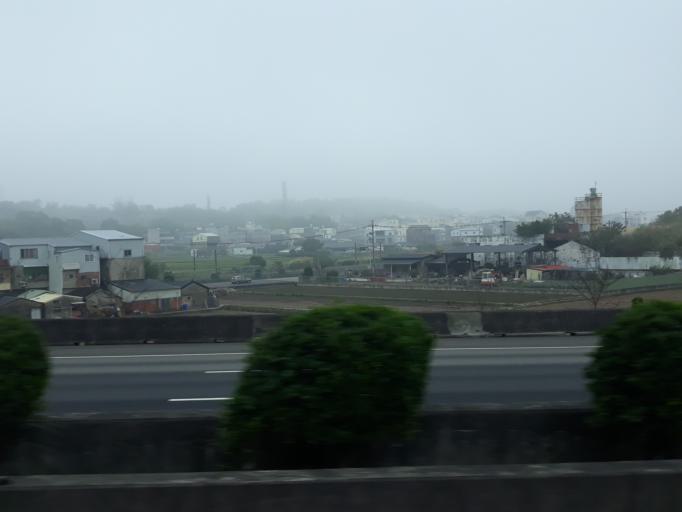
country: TW
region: Taiwan
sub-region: Miaoli
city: Miaoli
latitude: 24.4970
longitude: 120.7845
